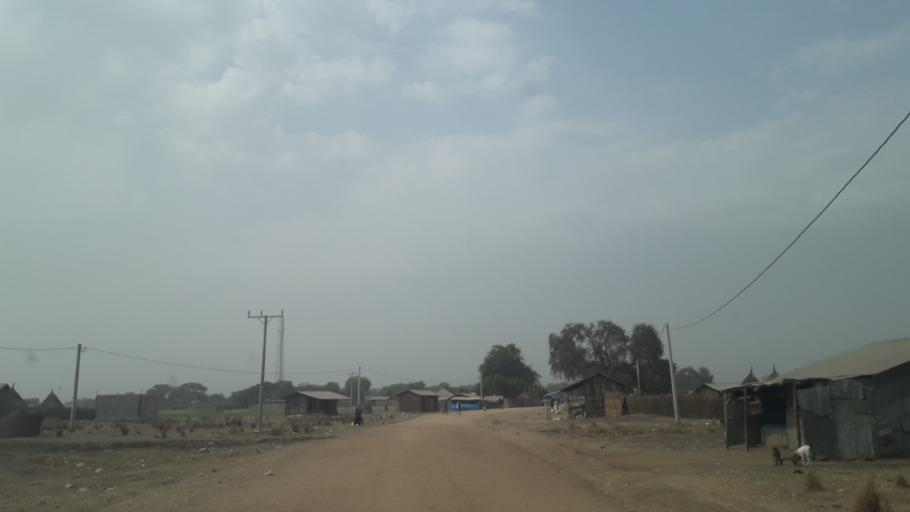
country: ET
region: Gambela
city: Gambela
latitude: 8.3050
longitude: 33.6860
